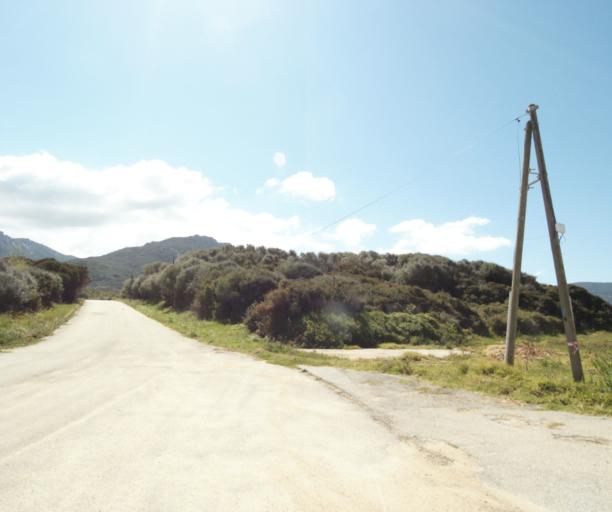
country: FR
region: Corsica
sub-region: Departement de la Corse-du-Sud
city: Propriano
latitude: 41.6588
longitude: 8.8934
